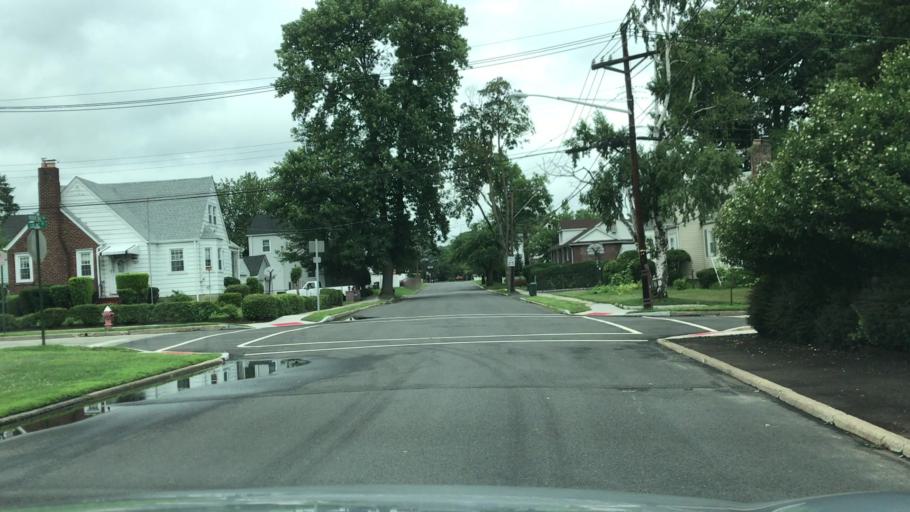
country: US
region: New Jersey
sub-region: Bergen County
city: Bergenfield
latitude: 40.9169
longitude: -73.9944
